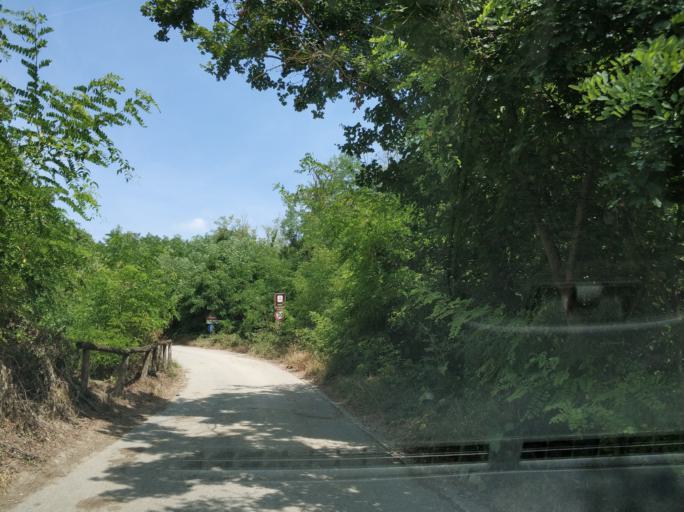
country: IT
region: Veneto
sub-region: Provincia di Padova
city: Arqua Petrarca
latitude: 45.2842
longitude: 11.7044
